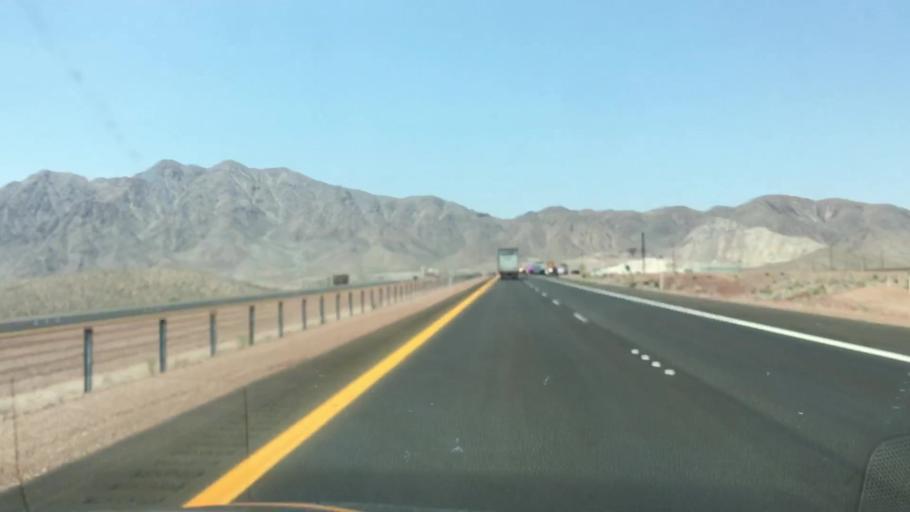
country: US
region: Nevada
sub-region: Clark County
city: Boulder City
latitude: 35.9506
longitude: -114.8982
